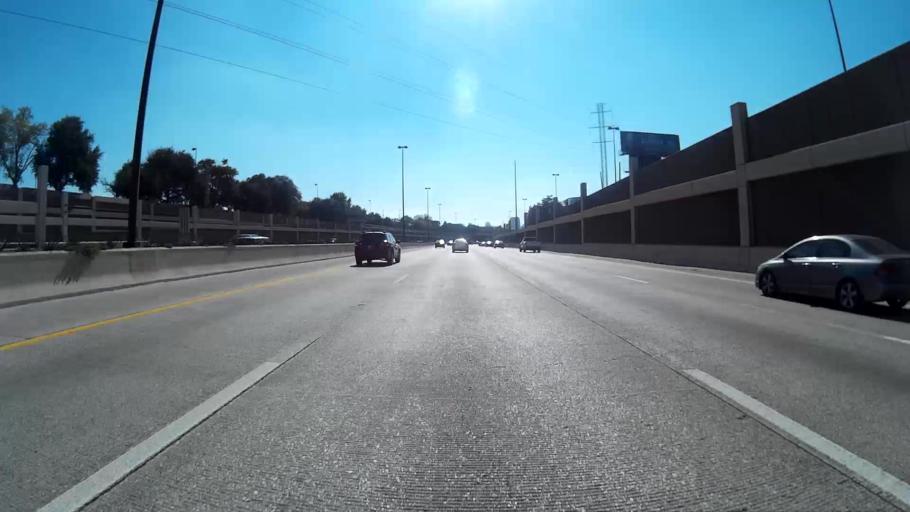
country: US
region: Texas
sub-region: Dallas County
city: Highland Park
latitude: 32.8337
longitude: -96.7802
